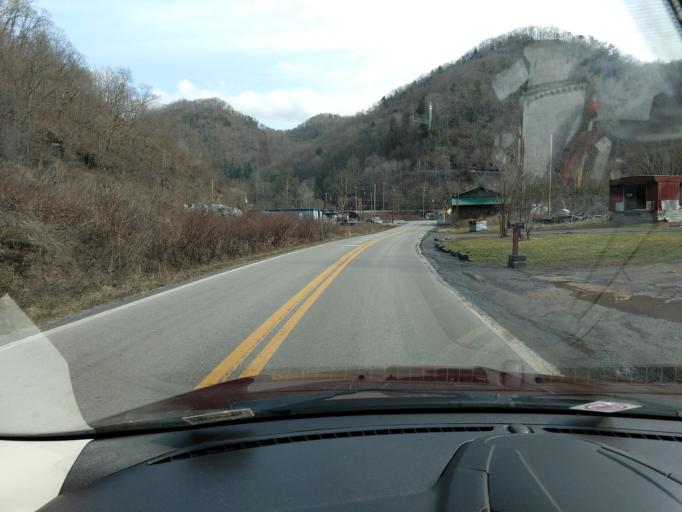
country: US
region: West Virginia
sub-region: McDowell County
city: Welch
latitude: 37.3215
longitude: -81.6983
